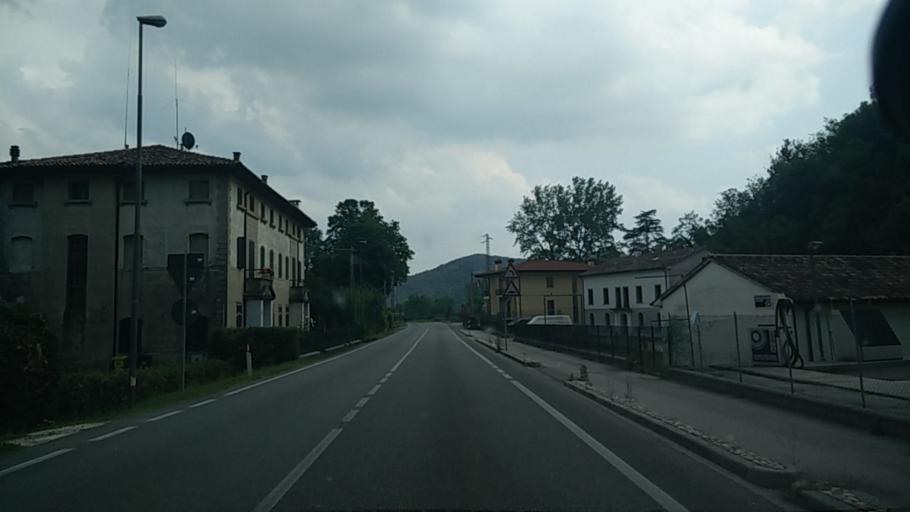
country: IT
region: Veneto
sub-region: Provincia di Treviso
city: Follina
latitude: 45.9473
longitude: 12.1231
